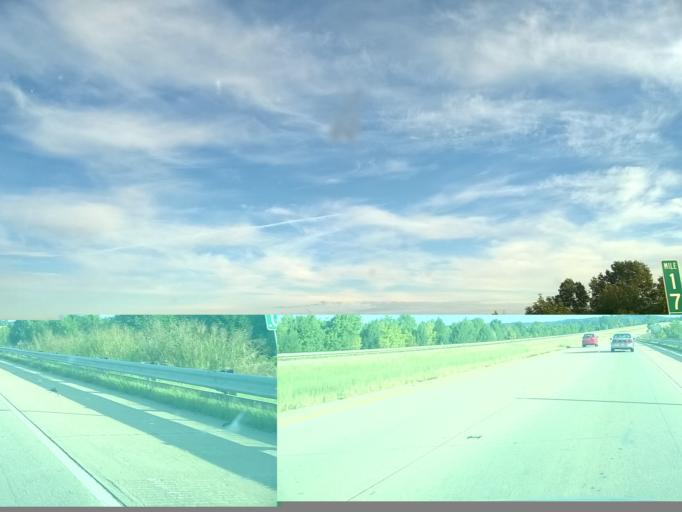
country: US
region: Indiana
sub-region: Vanderburgh County
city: Melody Hill
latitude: 38.1147
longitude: -87.4783
